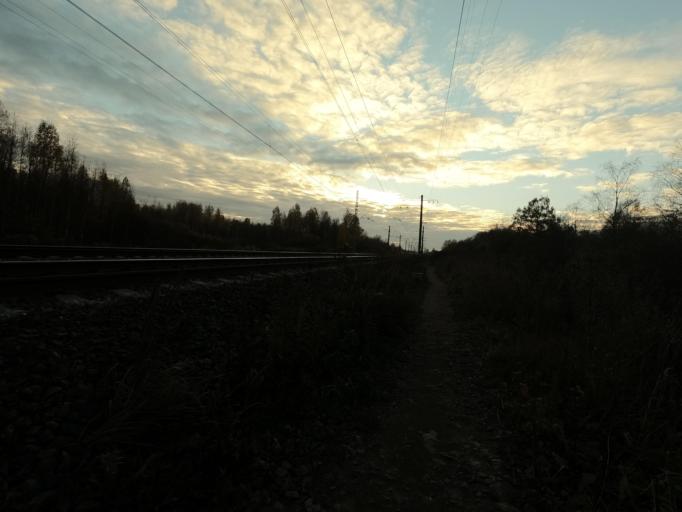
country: RU
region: Leningrad
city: Mga
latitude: 59.7751
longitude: 31.2223
